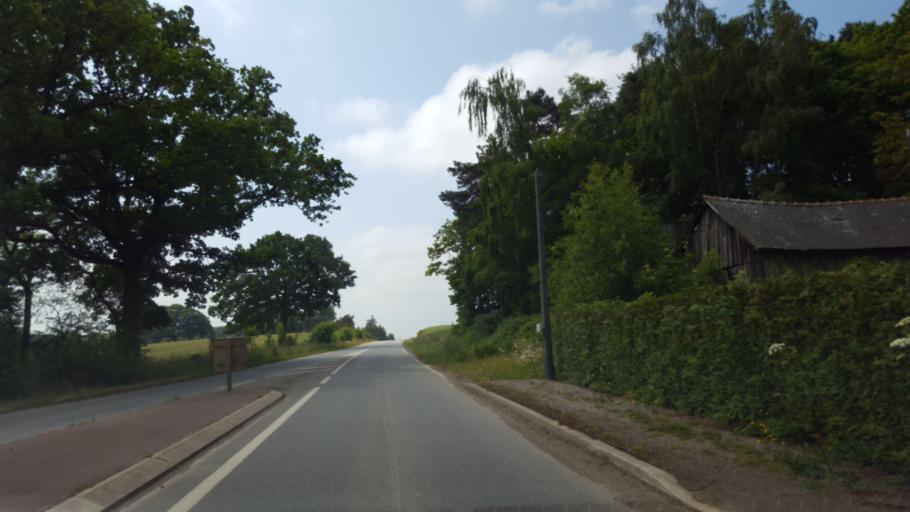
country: FR
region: Brittany
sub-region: Departement d'Ille-et-Vilaine
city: Maure-de-Bretagne
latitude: 47.9080
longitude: -1.9915
